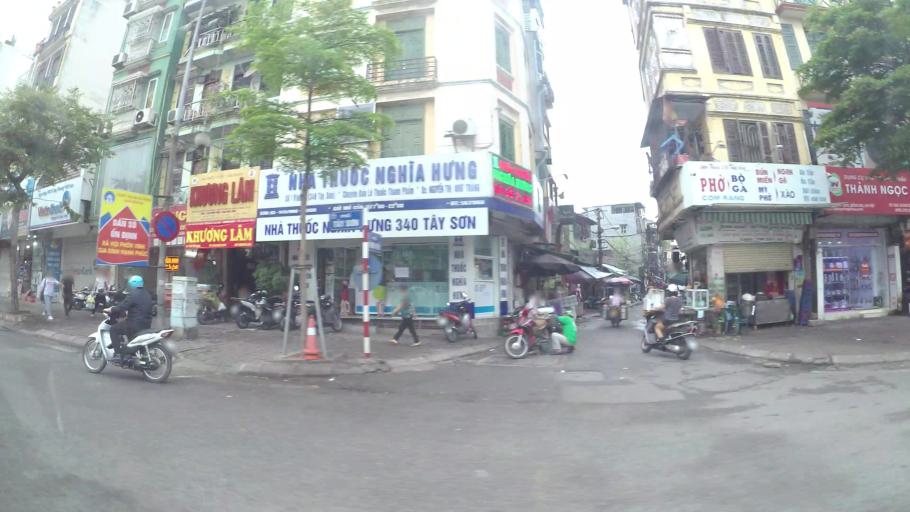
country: VN
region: Ha Noi
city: Dong Da
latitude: 21.0051
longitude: 105.8221
